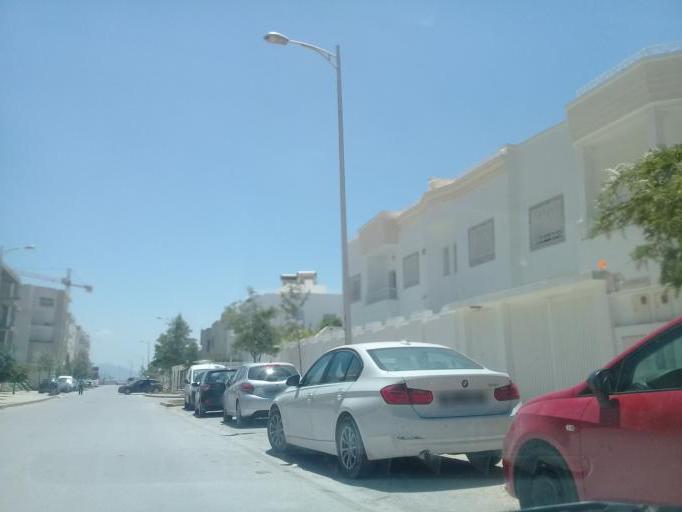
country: TN
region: Tunis
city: La Goulette
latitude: 36.8450
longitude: 10.2752
